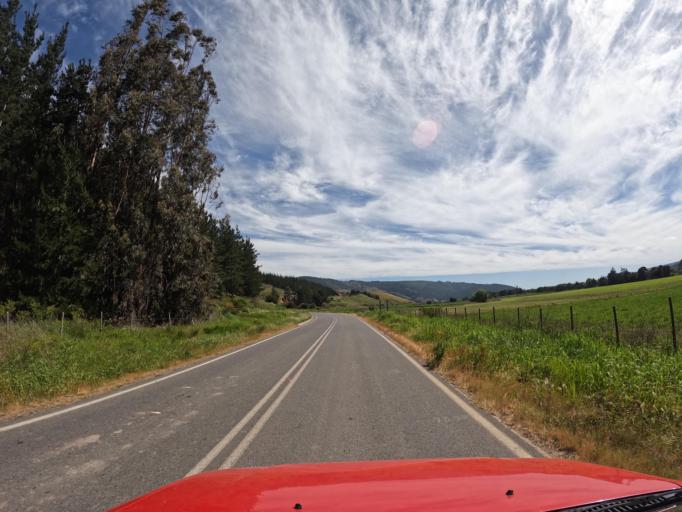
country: CL
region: Maule
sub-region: Provincia de Talca
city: Constitucion
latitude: -35.0372
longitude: -72.0566
